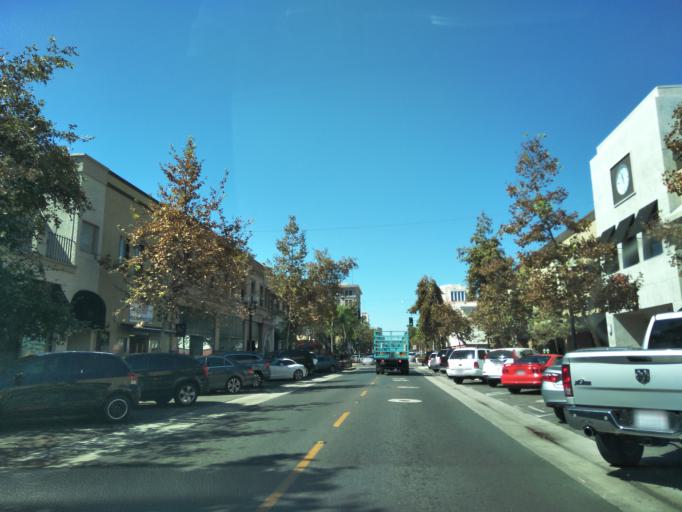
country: US
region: California
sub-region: Orange County
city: Santa Ana
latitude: 33.7480
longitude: -117.8659
